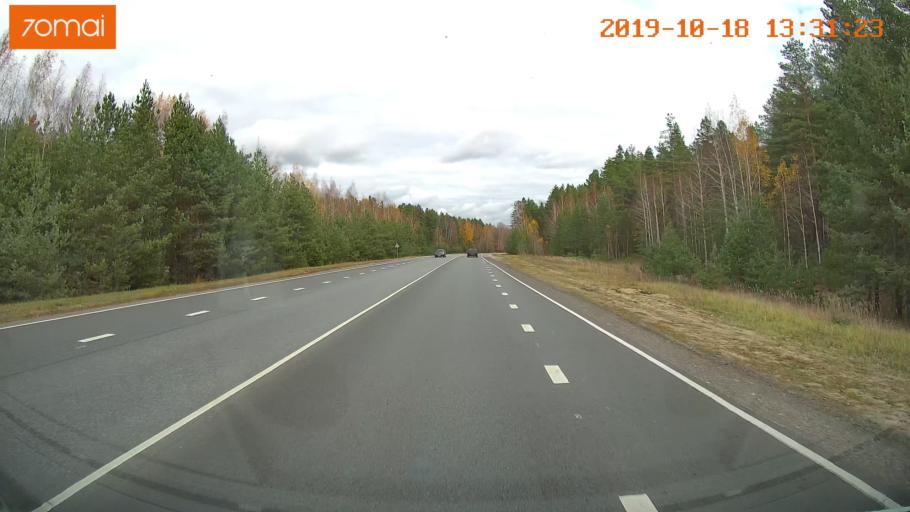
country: RU
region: Rjazan
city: Solotcha
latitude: 54.8217
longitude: 39.8991
